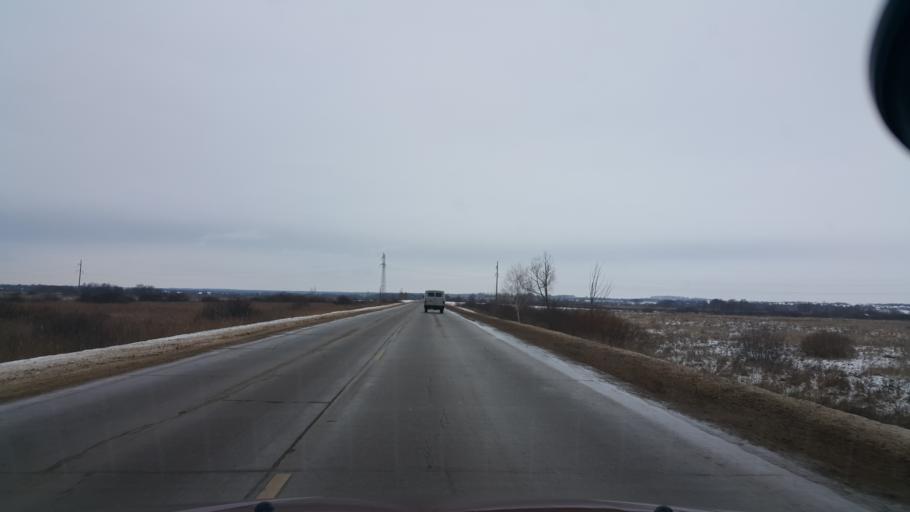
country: RU
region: Tambov
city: Bokino
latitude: 52.6238
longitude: 41.4857
